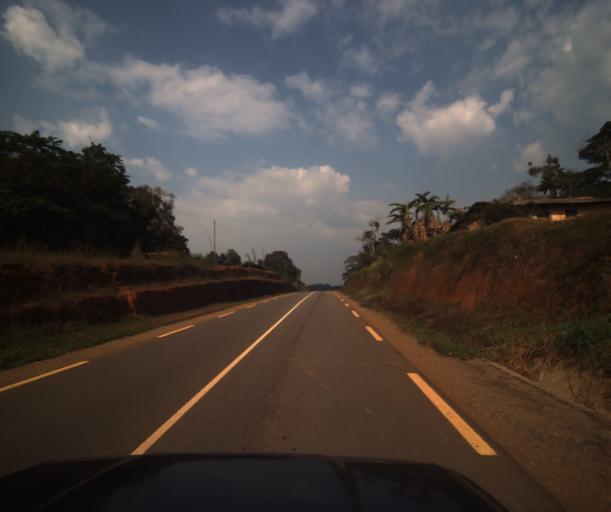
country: CM
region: Centre
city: Mbankomo
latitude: 3.6523
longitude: 11.3347
